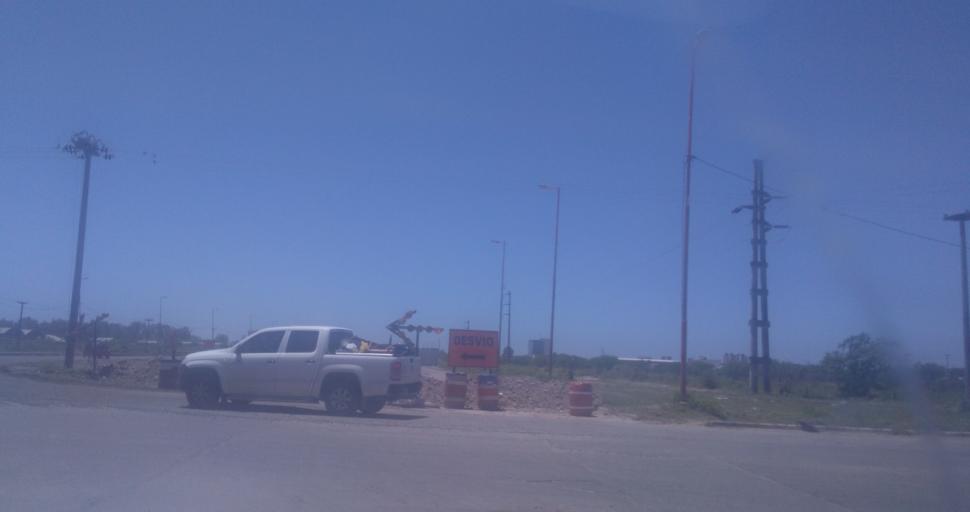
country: AR
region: Chaco
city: Fontana
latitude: -27.4517
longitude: -59.0293
